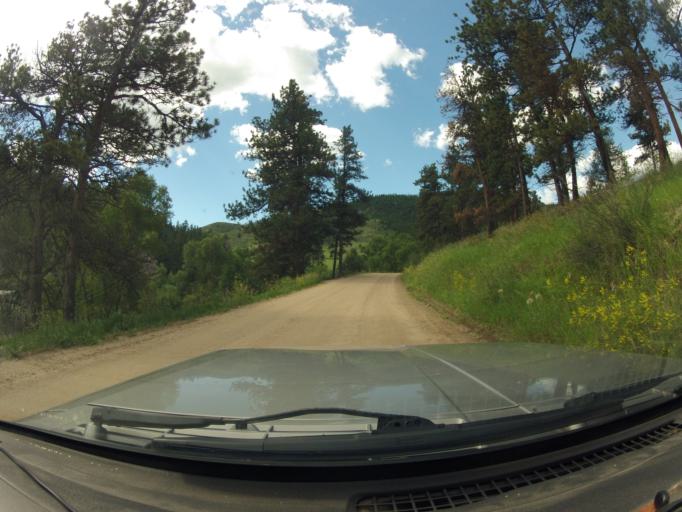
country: US
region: Colorado
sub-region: Larimer County
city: Laporte
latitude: 40.5727
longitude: -105.3296
